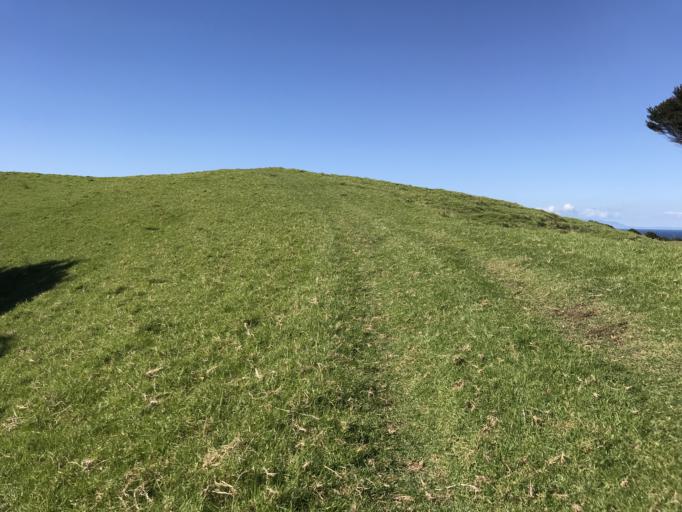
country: NZ
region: Auckland
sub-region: Auckland
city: Warkworth
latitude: -36.3752
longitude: 174.8320
